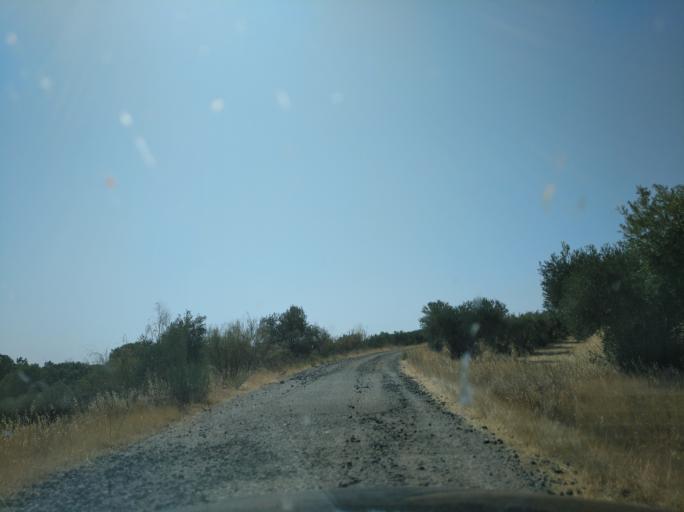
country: PT
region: Portalegre
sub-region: Campo Maior
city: Campo Maior
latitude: 39.0689
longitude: -7.0149
